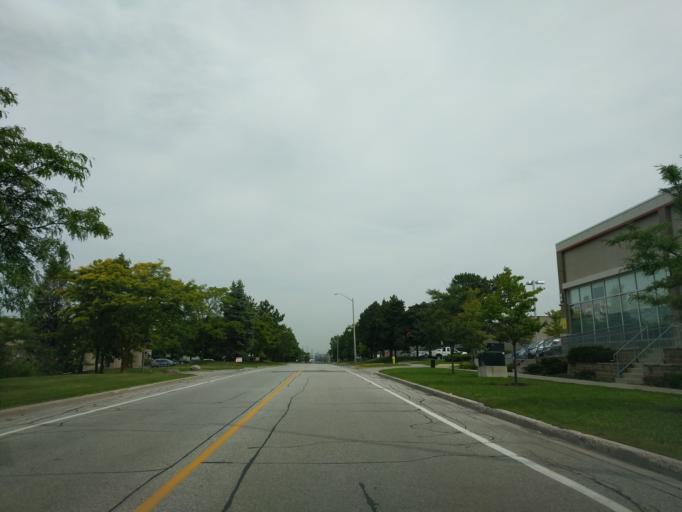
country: CA
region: Ontario
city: Markham
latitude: 43.8240
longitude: -79.3273
